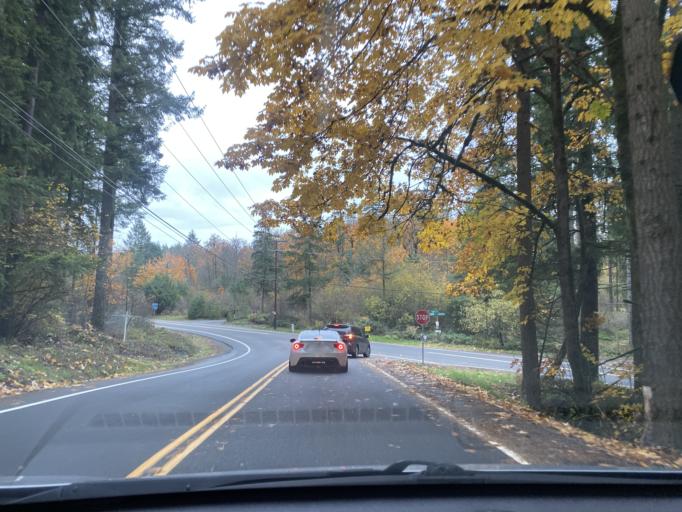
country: US
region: Washington
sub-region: King County
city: Lake Morton-Berrydale
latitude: 47.2998
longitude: -122.1027
